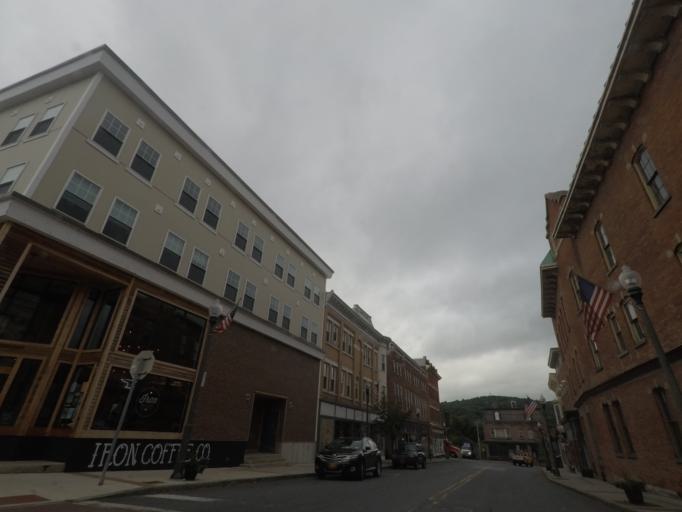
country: US
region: New York
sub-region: Rensselaer County
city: Hoosick Falls
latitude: 42.9014
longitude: -73.3507
